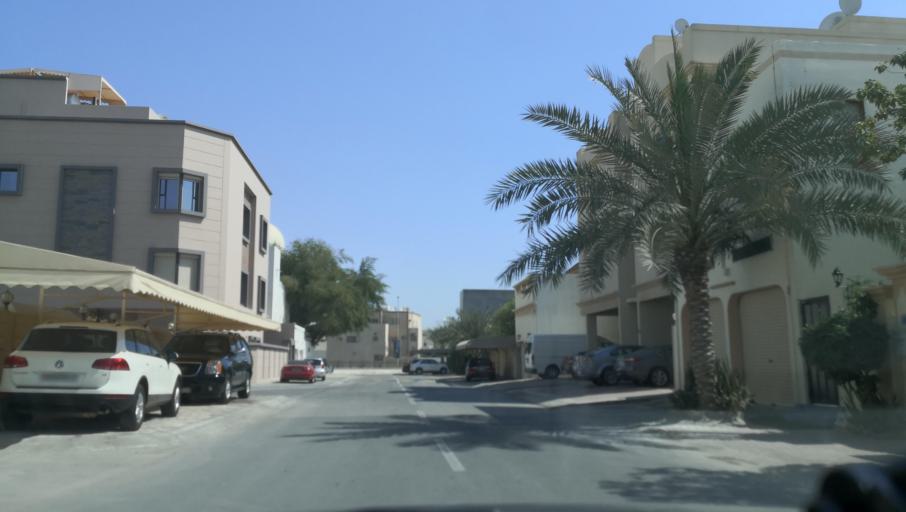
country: BH
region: Muharraq
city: Al Hadd
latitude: 26.2485
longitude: 50.6506
